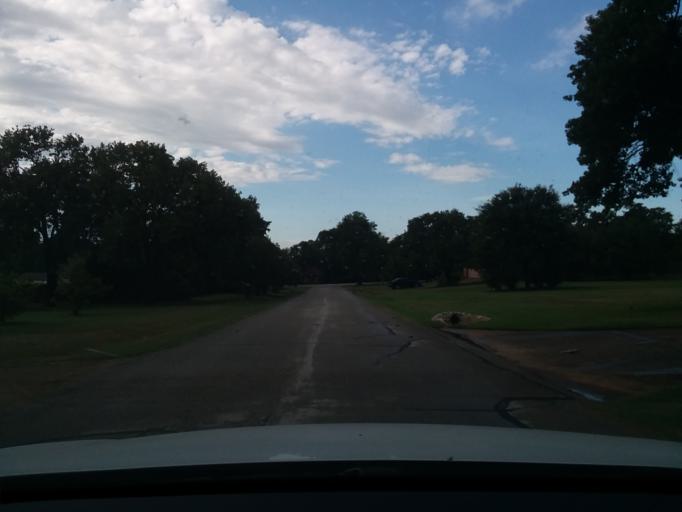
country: US
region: Texas
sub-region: Denton County
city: Double Oak
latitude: 33.0646
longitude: -97.1081
